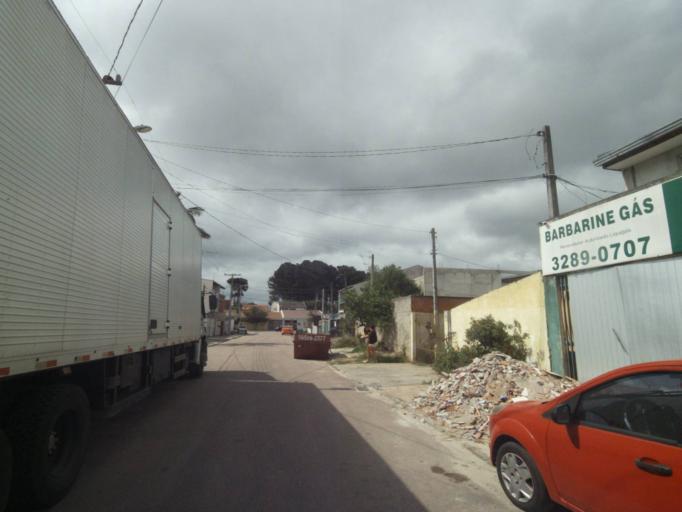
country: BR
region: Parana
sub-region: Sao Jose Dos Pinhais
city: Sao Jose dos Pinhais
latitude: -25.5468
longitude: -49.2728
